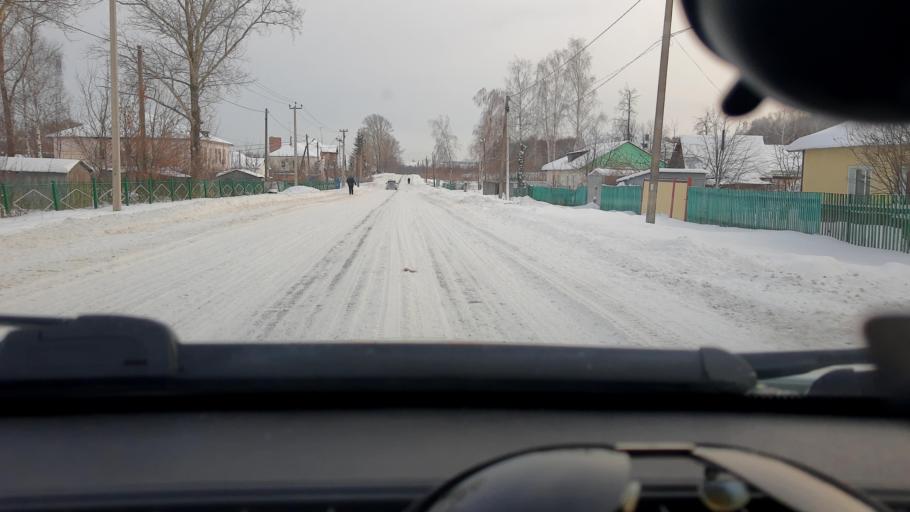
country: RU
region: Bashkortostan
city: Yazykovo
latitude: 55.0454
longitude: 56.1821
